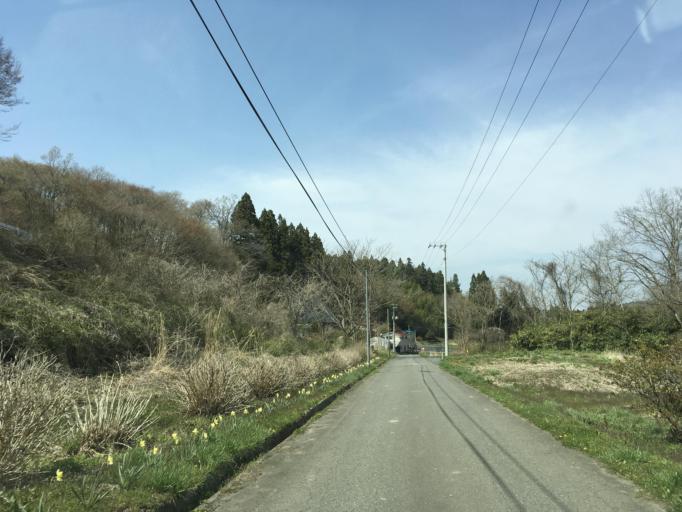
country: JP
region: Iwate
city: Ichinoseki
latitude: 38.8309
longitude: 141.3513
